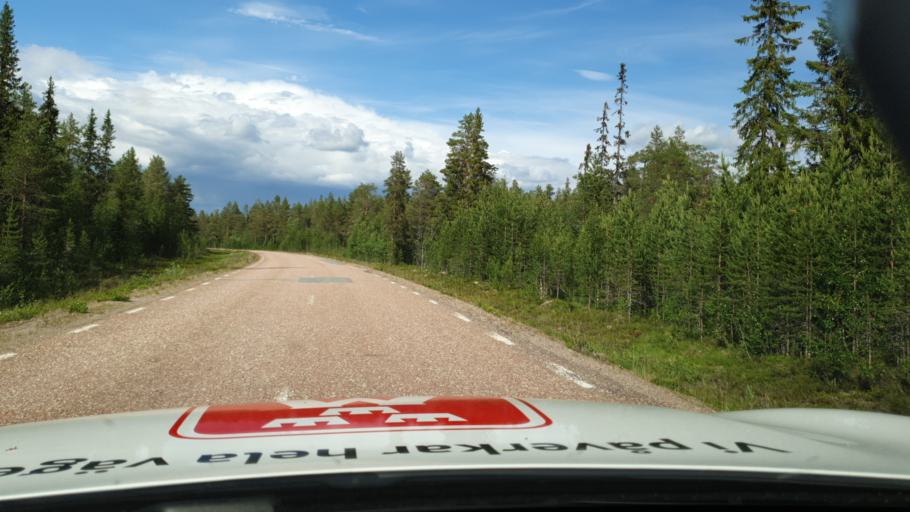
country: SE
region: Dalarna
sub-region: Alvdalens Kommun
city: AElvdalen
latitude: 61.7700
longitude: 13.4818
